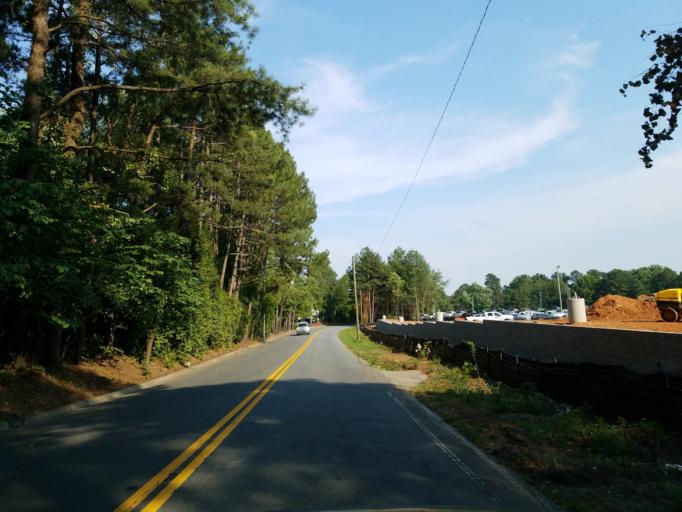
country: US
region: Georgia
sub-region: Cobb County
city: Fair Oaks
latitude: 33.9354
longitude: -84.5083
